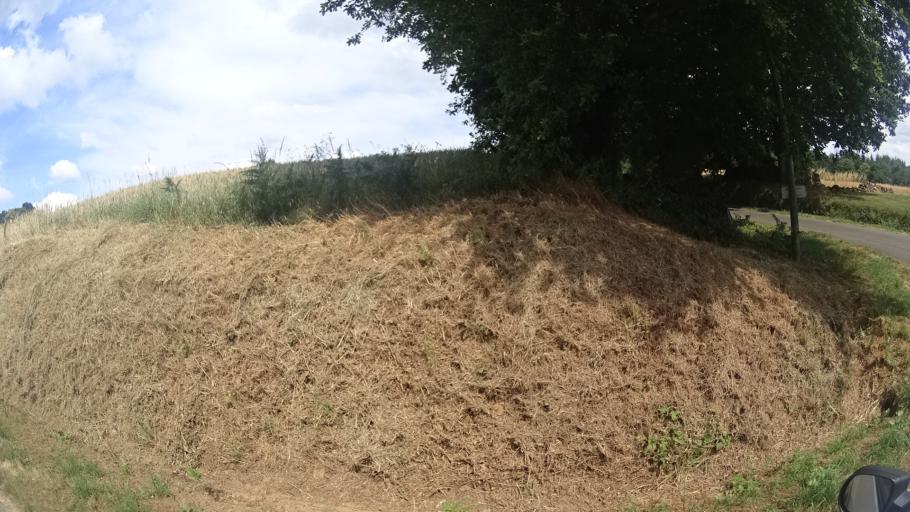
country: FR
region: Brittany
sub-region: Departement du Morbihan
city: Peillac
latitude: 47.7053
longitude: -2.2177
